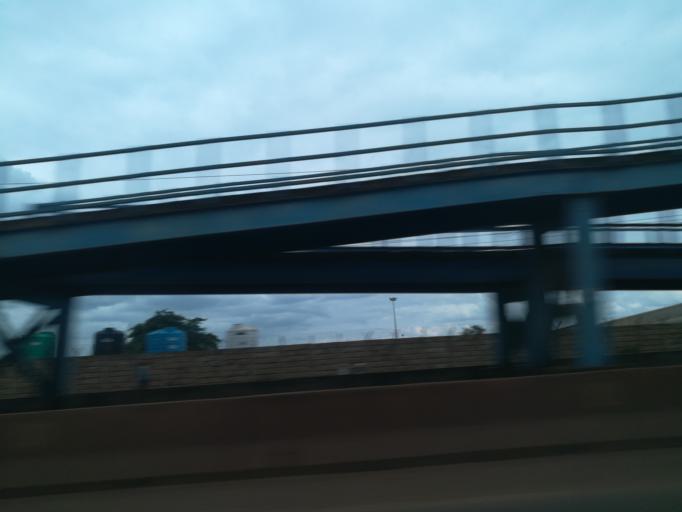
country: KE
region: Nairobi Area
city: Thika
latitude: -1.0530
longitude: 37.0569
